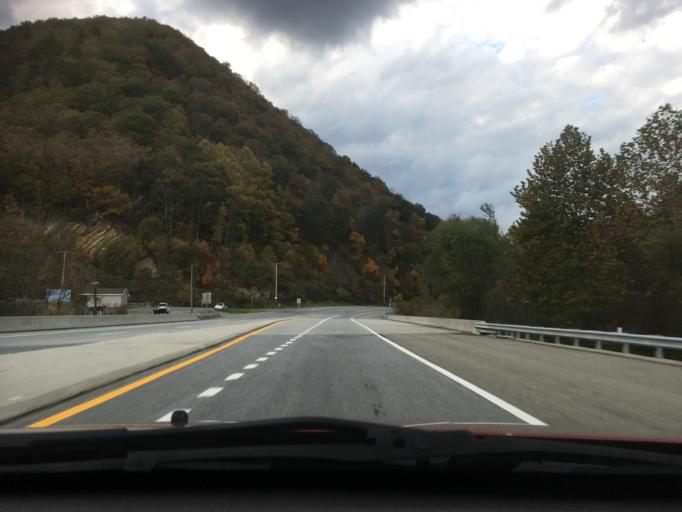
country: US
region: Virginia
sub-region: Pulaski County
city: Dublin
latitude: 37.1966
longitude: -80.7325
